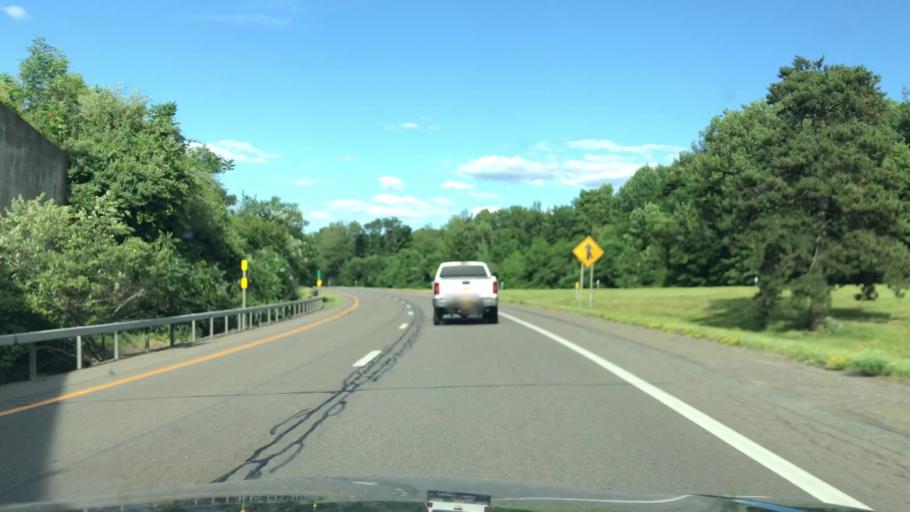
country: US
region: New York
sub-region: Broome County
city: Chenango Bridge
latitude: 42.0994
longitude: -75.8140
